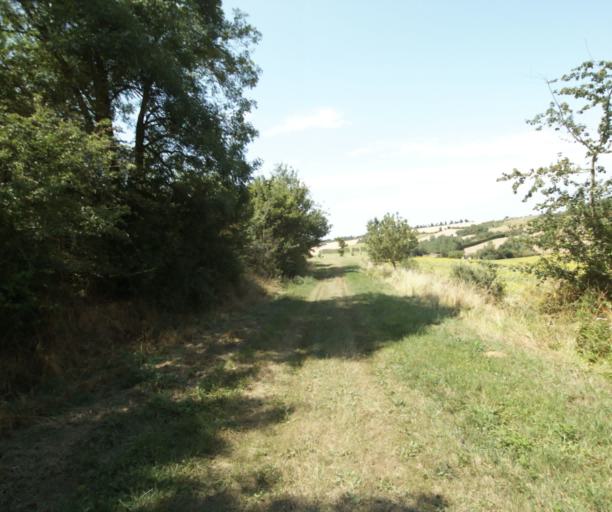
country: FR
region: Midi-Pyrenees
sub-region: Departement de la Haute-Garonne
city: Saint-Felix-Lauragais
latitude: 43.4515
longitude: 1.8839
